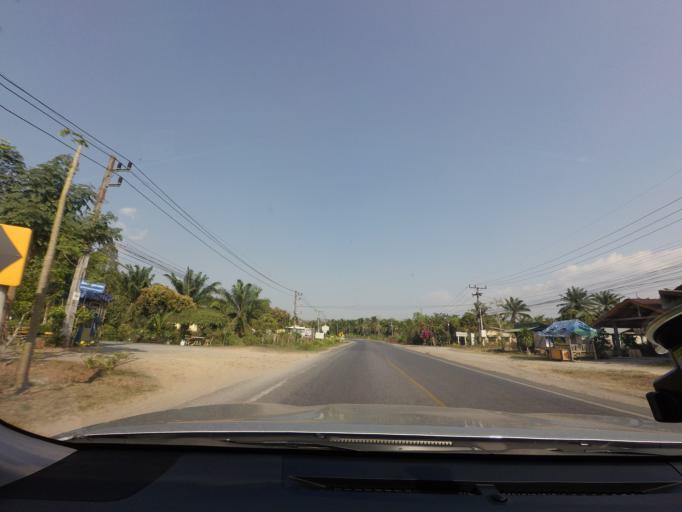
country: TH
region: Surat Thani
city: Phrasaeng
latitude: 8.5591
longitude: 99.1716
